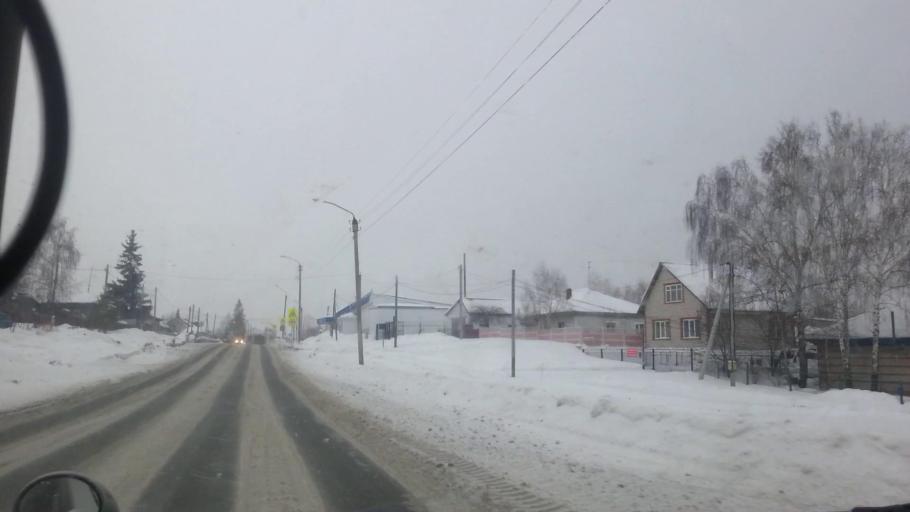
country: RU
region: Altai Krai
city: Vlasikha
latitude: 53.2956
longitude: 83.5805
